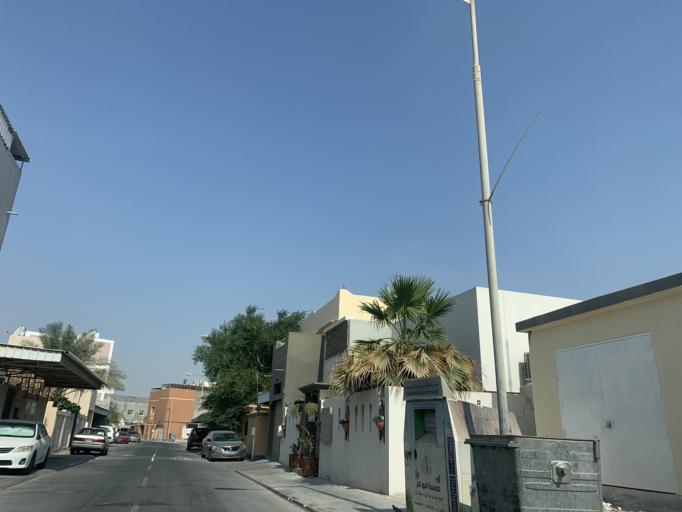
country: BH
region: Central Governorate
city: Madinat Hamad
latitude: 26.1219
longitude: 50.4926
